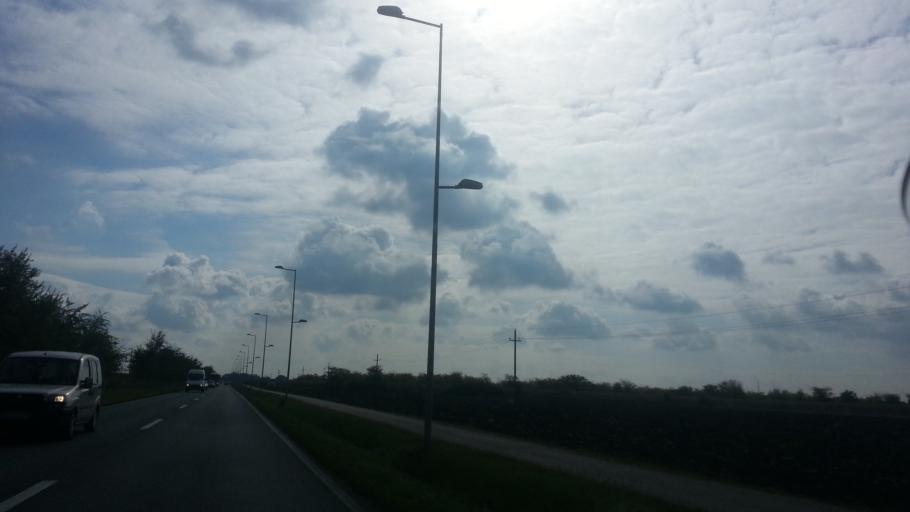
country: RS
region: Autonomna Pokrajina Vojvodina
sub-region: Sremski Okrug
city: Stara Pazova
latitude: 44.9640
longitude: 20.1886
